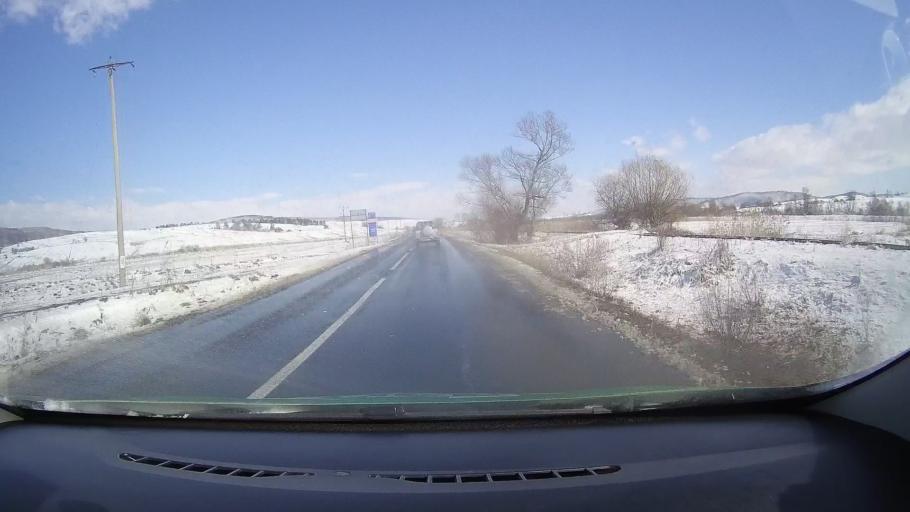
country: RO
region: Sibiu
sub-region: Comuna Rosia
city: Rosia
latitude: 45.8060
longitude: 24.3553
